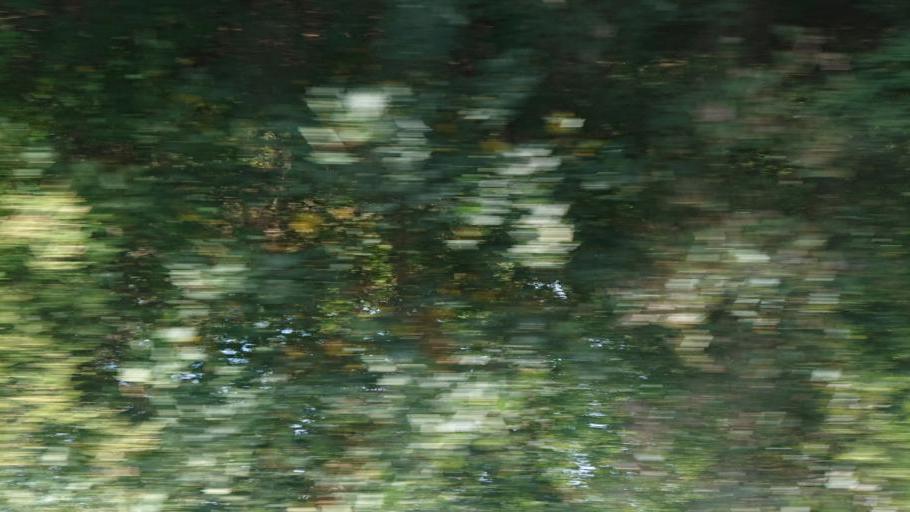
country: DE
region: Brandenburg
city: Gramzow
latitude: 53.2523
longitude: 13.9629
